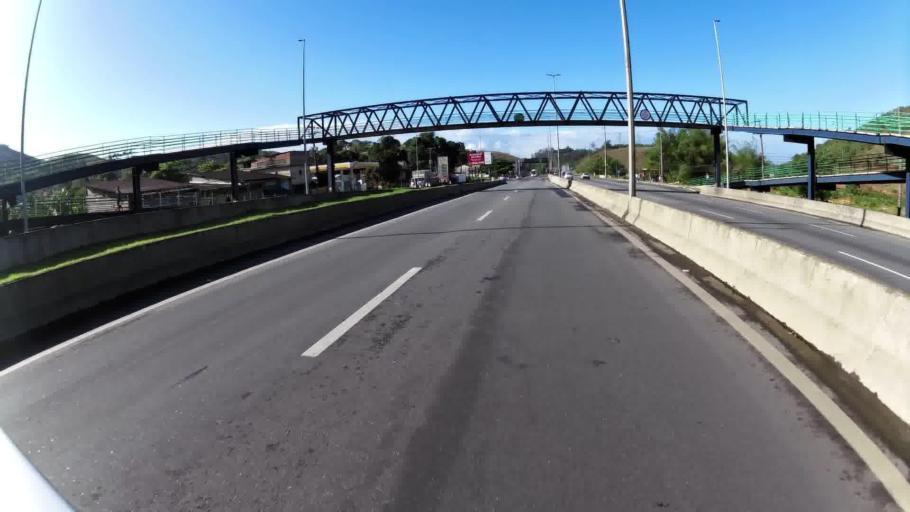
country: BR
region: Rio de Janeiro
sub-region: Petropolis
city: Petropolis
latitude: -22.6150
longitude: -43.2868
